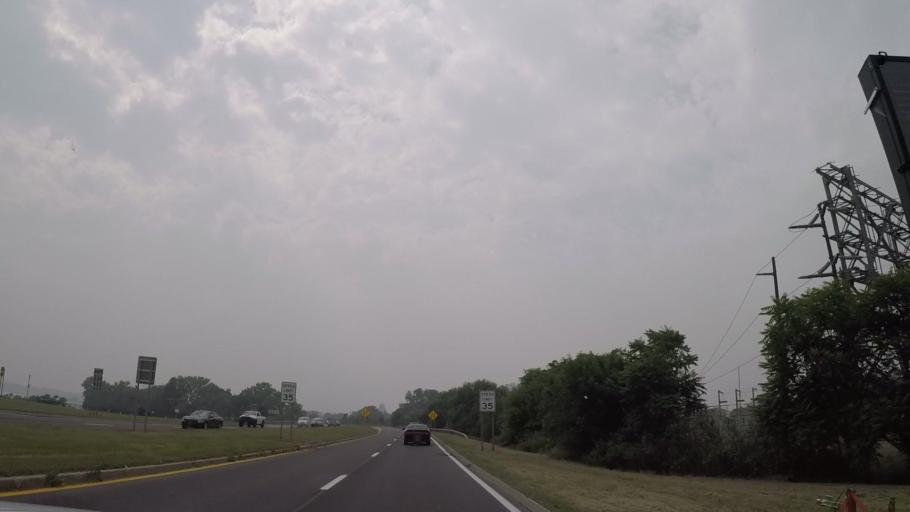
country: US
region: New York
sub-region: Niagara County
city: Niagara Falls
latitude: 43.0793
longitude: -79.0442
